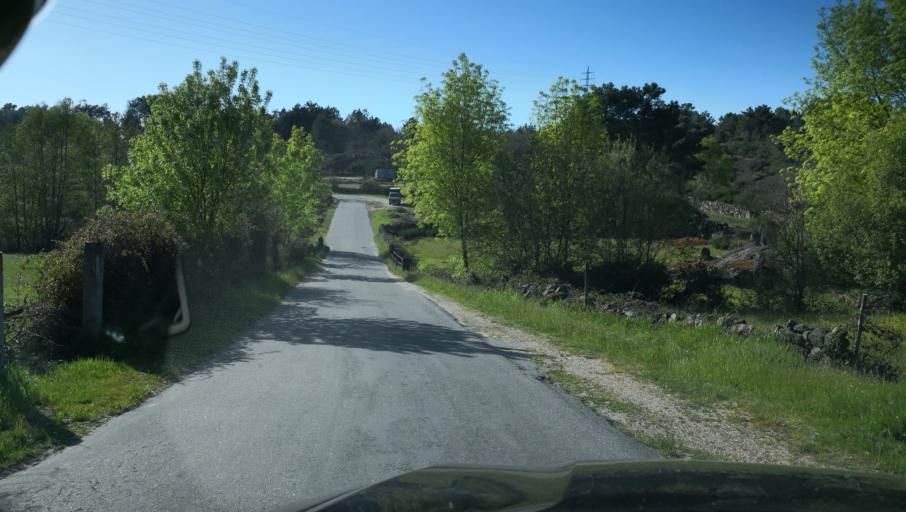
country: PT
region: Vila Real
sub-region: Vila Real
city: Vila Real
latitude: 41.2937
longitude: -7.6653
